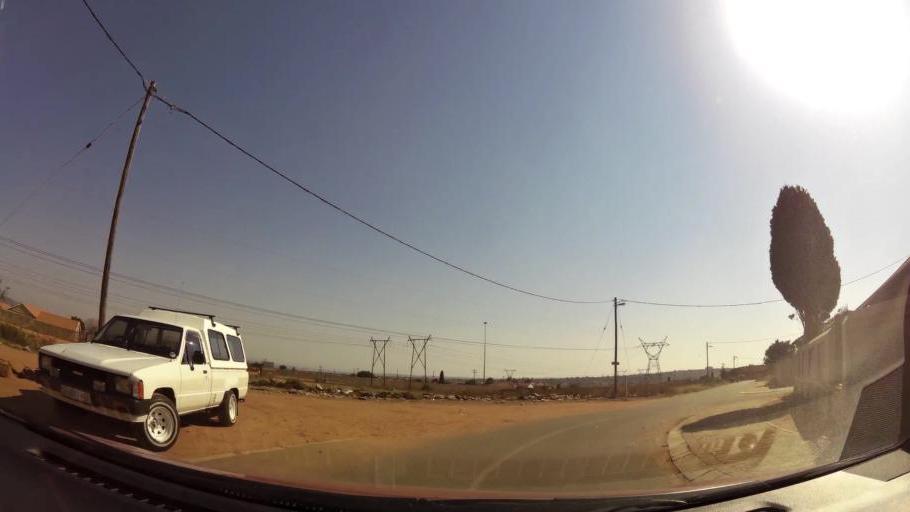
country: ZA
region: Gauteng
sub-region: City of Tshwane Metropolitan Municipality
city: Mabopane
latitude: -25.5538
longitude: 28.0798
